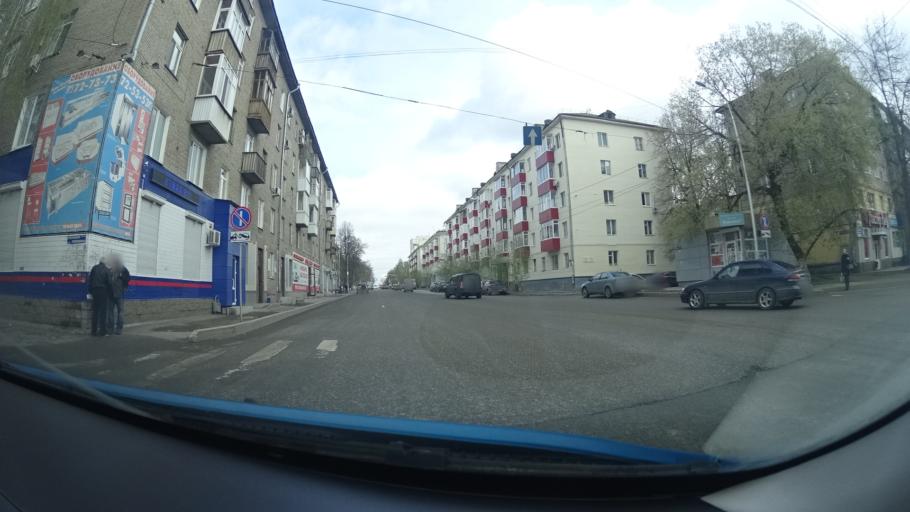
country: RU
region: Bashkortostan
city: Ufa
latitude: 54.7339
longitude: 55.9628
